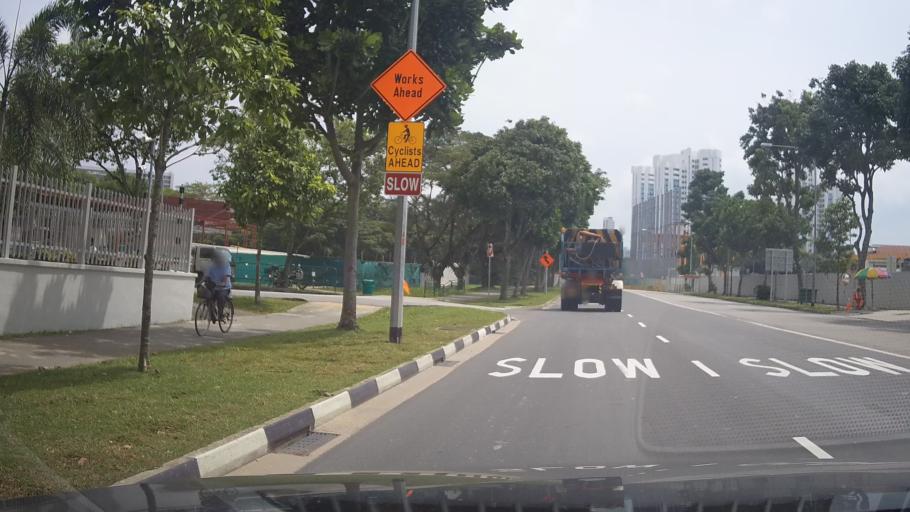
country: SG
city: Singapore
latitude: 1.2976
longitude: 103.8780
